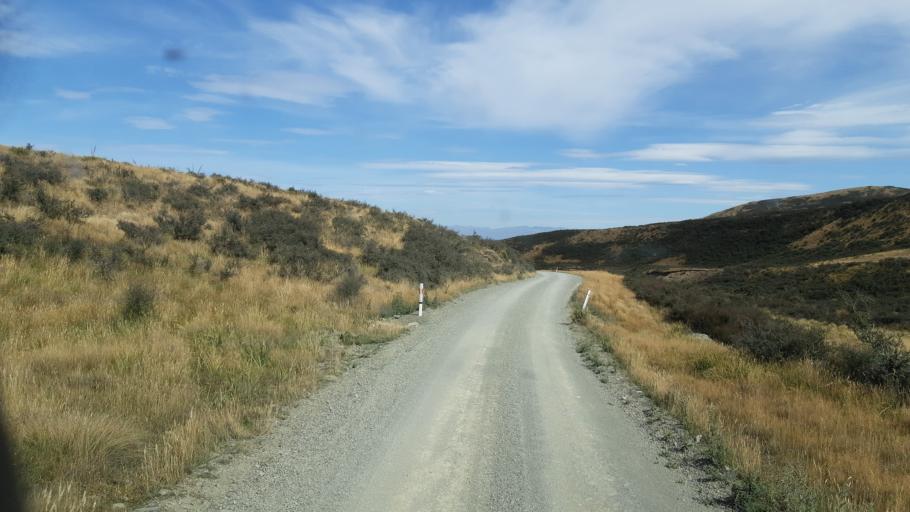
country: NZ
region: Canterbury
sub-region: Timaru District
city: Pleasant Point
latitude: -44.1943
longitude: 170.5896
